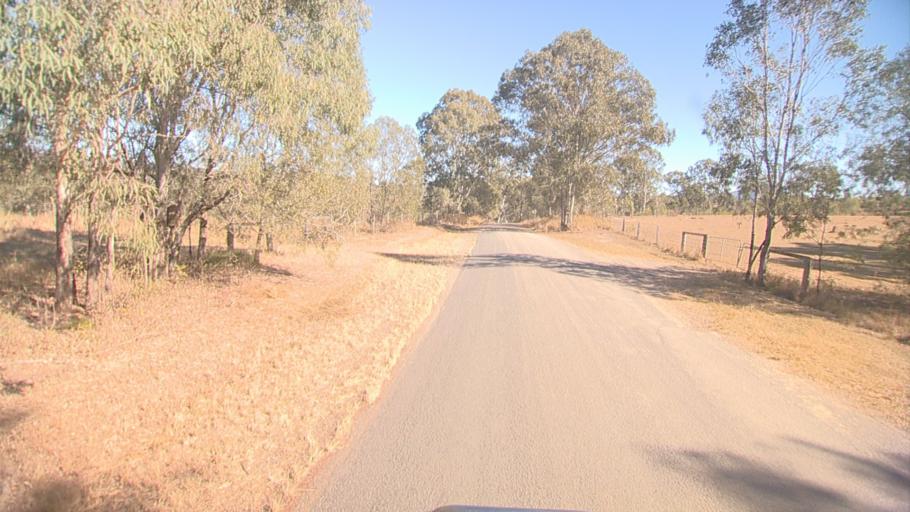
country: AU
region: Queensland
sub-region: Logan
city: Cedar Vale
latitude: -27.8477
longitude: 152.8918
